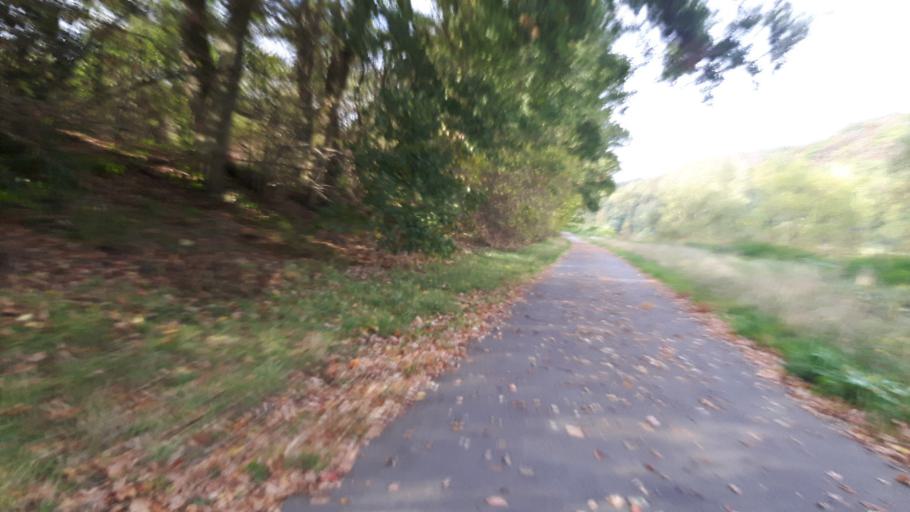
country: DE
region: Rheinland-Pfalz
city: Werkhausen
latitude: 50.7624
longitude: 7.5266
